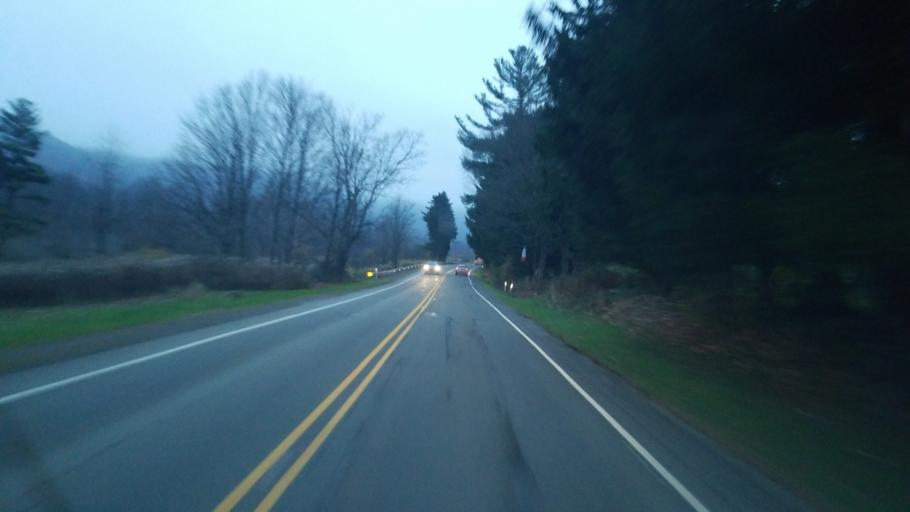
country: US
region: Pennsylvania
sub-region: McKean County
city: Smethport
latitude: 41.7721
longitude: -78.5118
